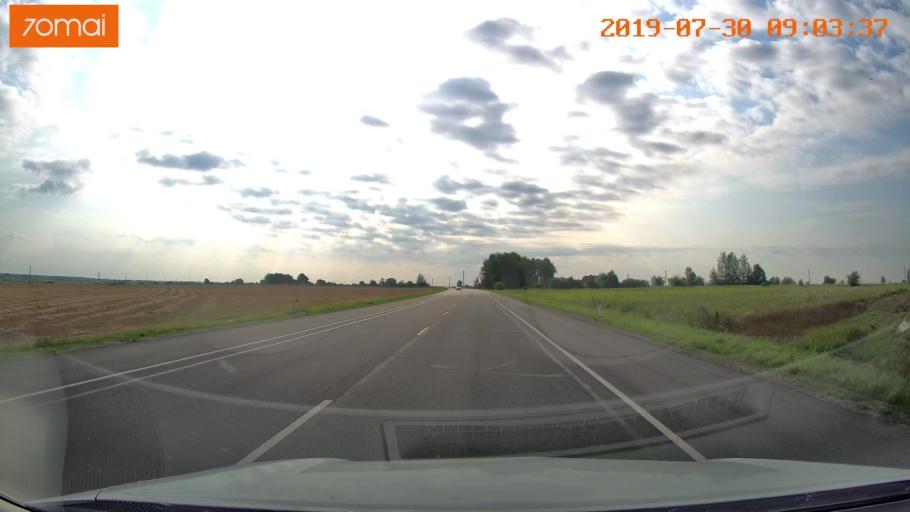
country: RU
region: Kaliningrad
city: Gusev
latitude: 54.6067
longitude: 22.2581
